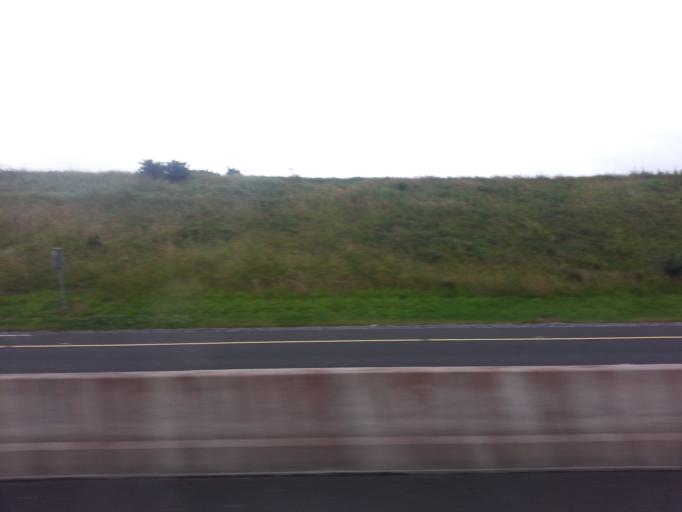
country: IE
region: Leinster
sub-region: Kilkenny
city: Thomastown
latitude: 52.6528
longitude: -7.0957
